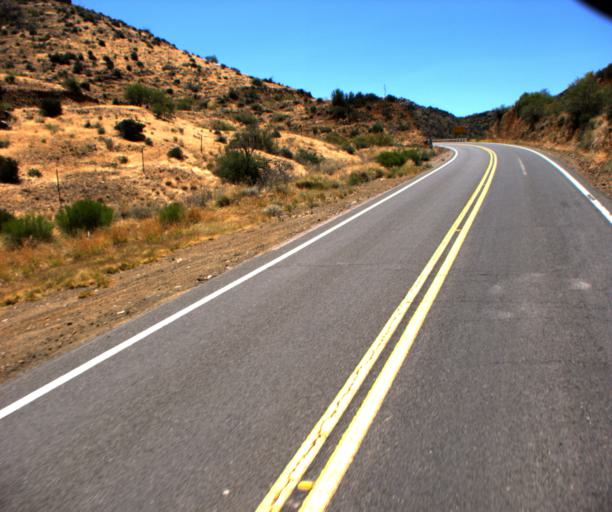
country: US
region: Arizona
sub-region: Pinal County
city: Superior
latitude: 33.2083
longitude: -111.0601
